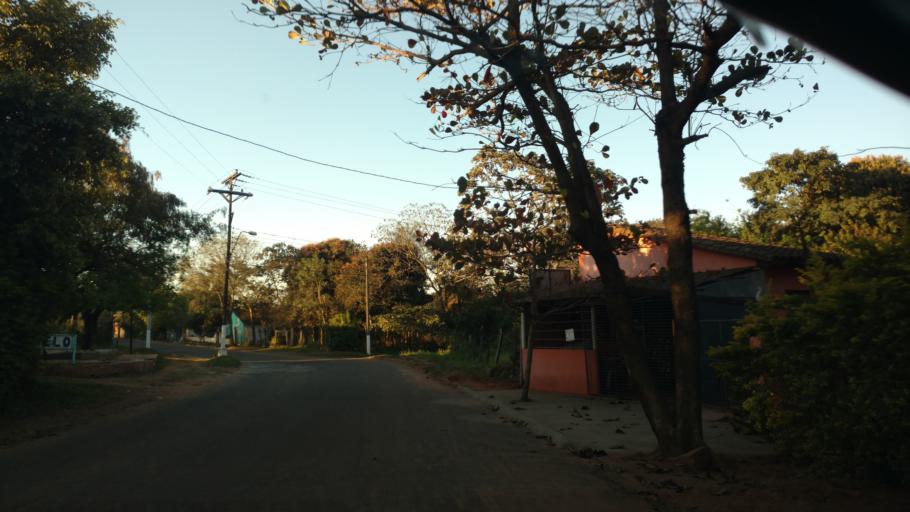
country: PY
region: Paraguari
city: Yaguaron
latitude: -25.5675
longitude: -57.2852
